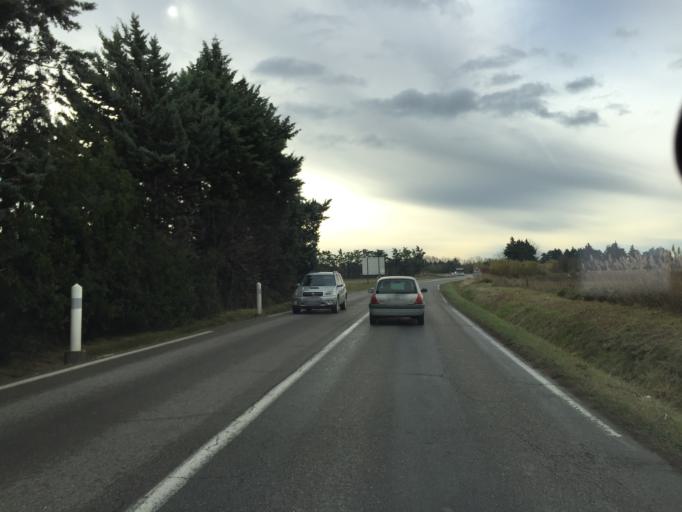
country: FR
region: Provence-Alpes-Cote d'Azur
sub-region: Departement du Vaucluse
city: L'Isle-sur-la-Sorgue
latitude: 43.8957
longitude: 5.0464
